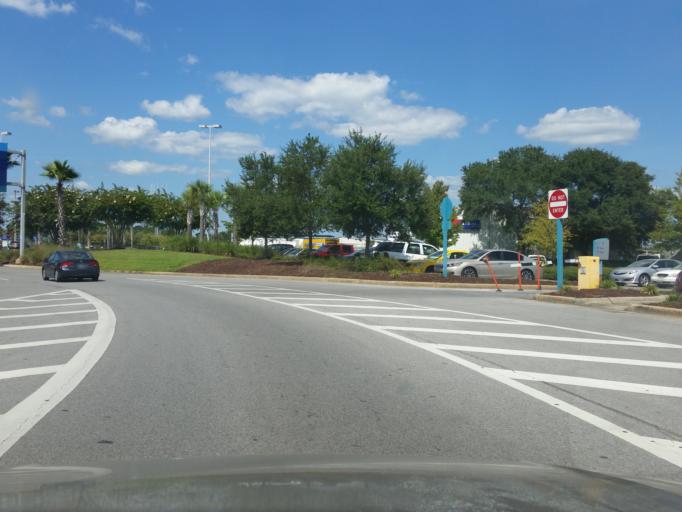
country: US
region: Florida
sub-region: Escambia County
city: Ferry Pass
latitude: 30.4772
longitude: -87.1935
